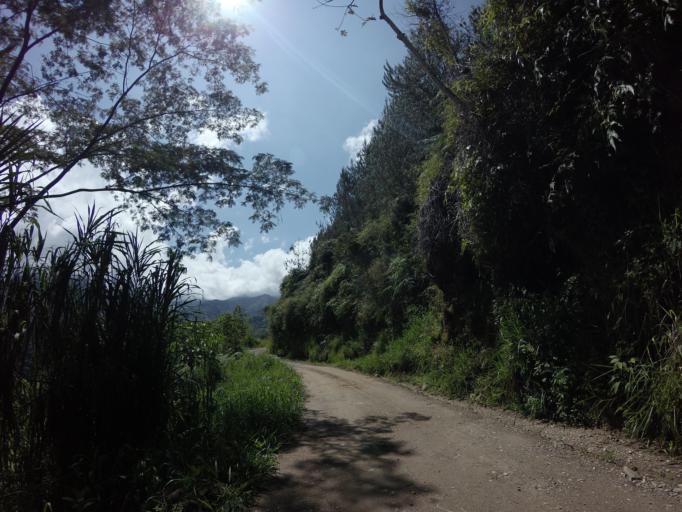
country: CO
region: Caldas
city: Pensilvania
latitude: 5.4852
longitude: -75.1764
